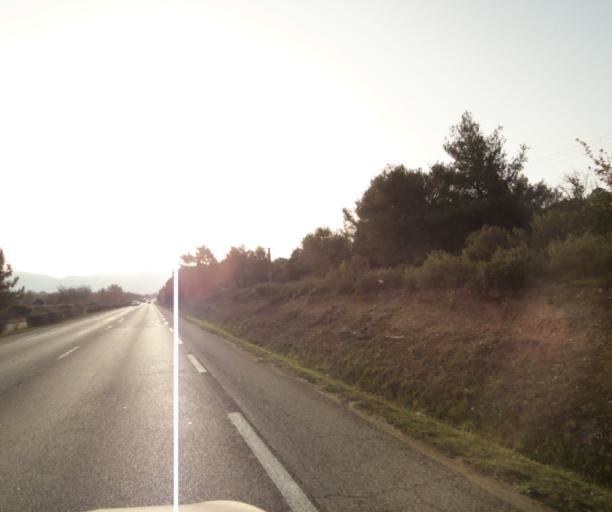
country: FR
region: Provence-Alpes-Cote d'Azur
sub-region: Departement des Bouches-du-Rhone
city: Peynier
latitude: 43.4567
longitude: 5.6597
